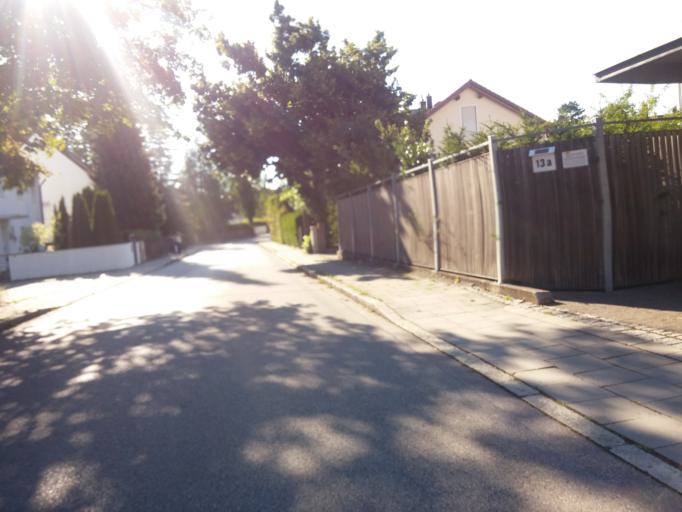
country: DE
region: Bavaria
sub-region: Upper Bavaria
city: Vaterstetten
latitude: 48.1007
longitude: 11.7910
